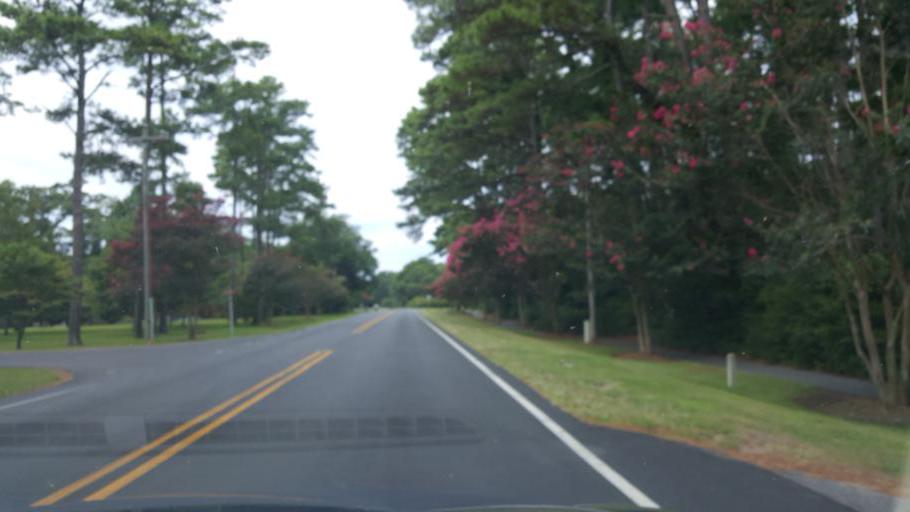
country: US
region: North Carolina
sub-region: Dare County
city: Manteo
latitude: 35.9337
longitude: -75.6984
